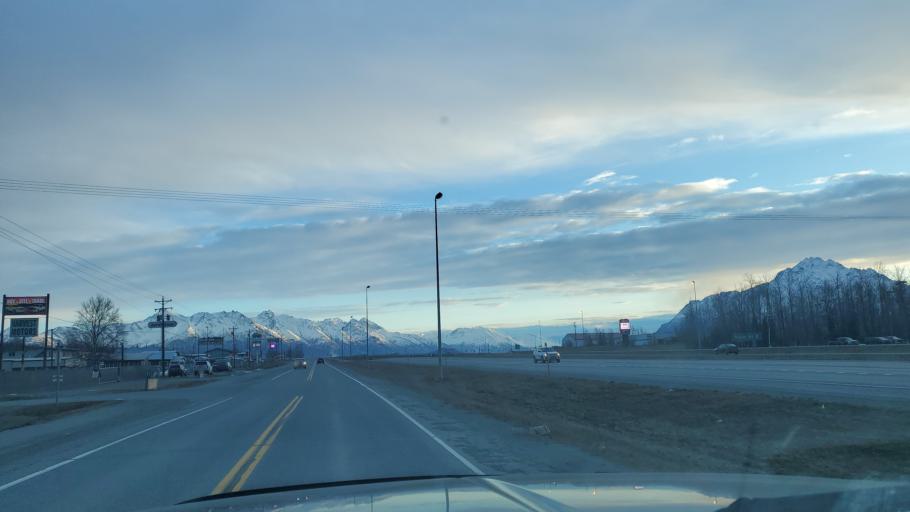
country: US
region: Alaska
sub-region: Matanuska-Susitna Borough
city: Gateway
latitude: 61.5633
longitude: -149.2776
